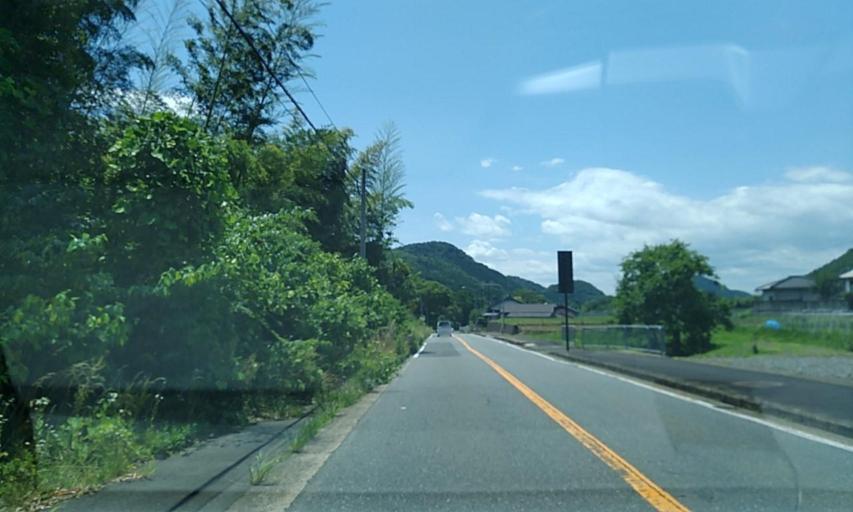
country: JP
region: Kyoto
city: Ayabe
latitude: 35.2879
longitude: 135.2915
